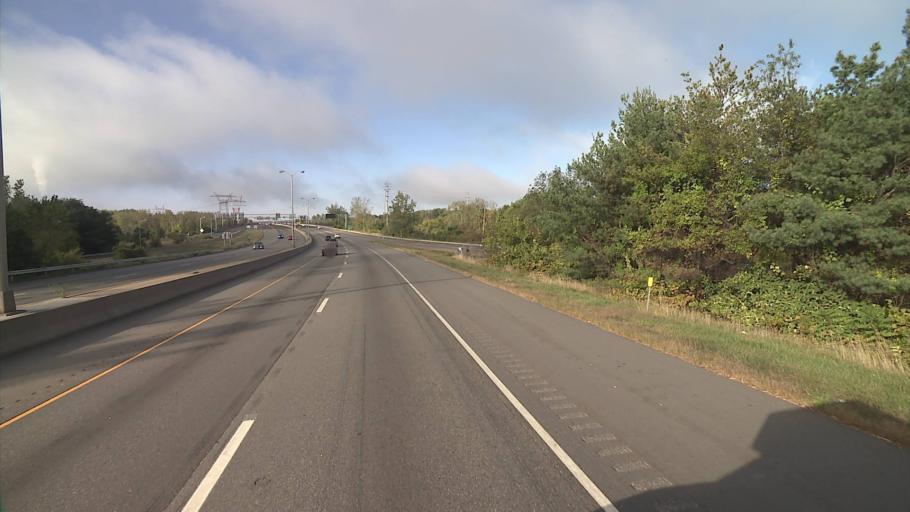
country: US
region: Connecticut
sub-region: Hartford County
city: Hartford
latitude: 41.7578
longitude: -72.6467
